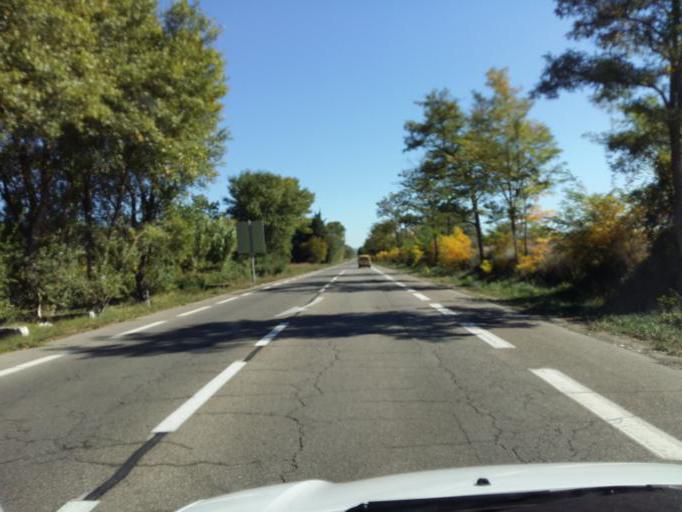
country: FR
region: Provence-Alpes-Cote d'Azur
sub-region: Departement des Bouches-du-Rhone
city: Charleval
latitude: 43.7505
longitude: 5.2704
